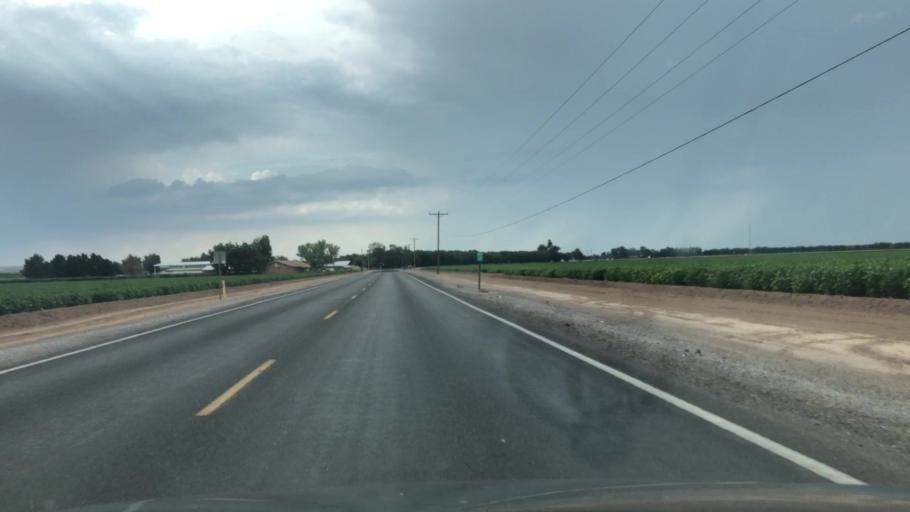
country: US
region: New Mexico
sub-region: Dona Ana County
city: La Union
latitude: 31.9665
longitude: -106.6495
